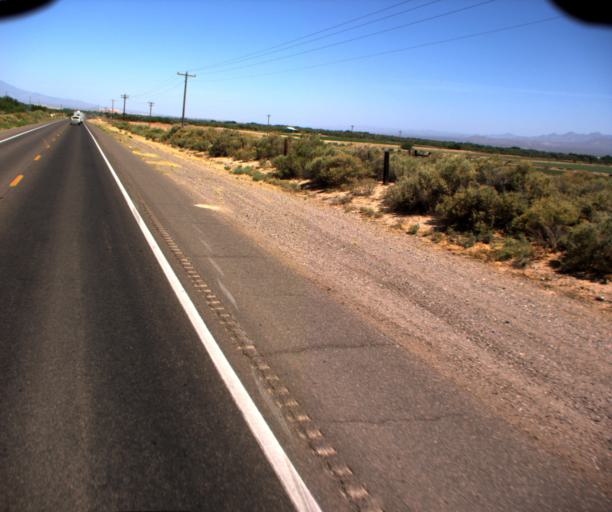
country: US
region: Arizona
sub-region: Graham County
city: Pima
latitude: 32.9274
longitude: -109.8825
